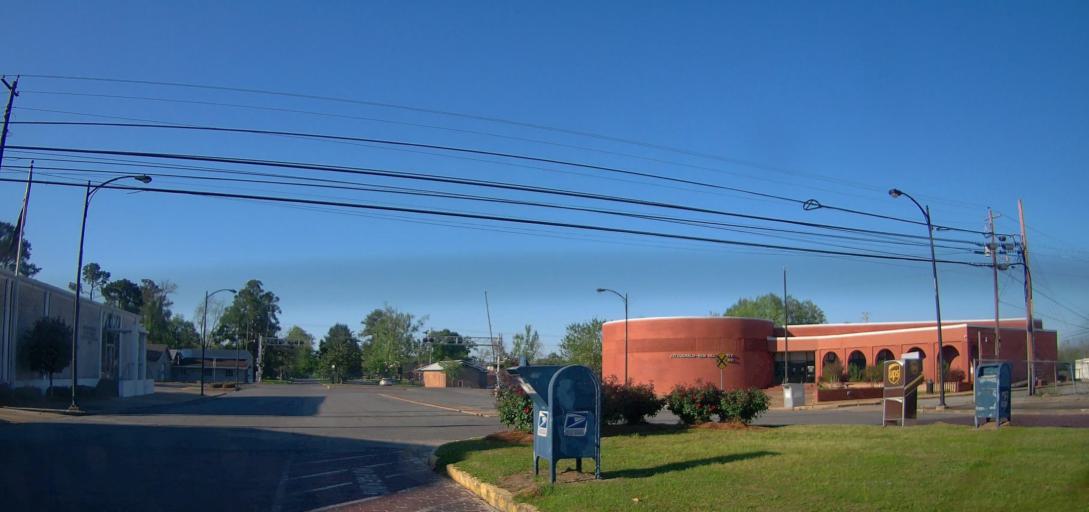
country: US
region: Georgia
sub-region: Ben Hill County
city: Fitzgerald
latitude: 31.7154
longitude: -83.2543
